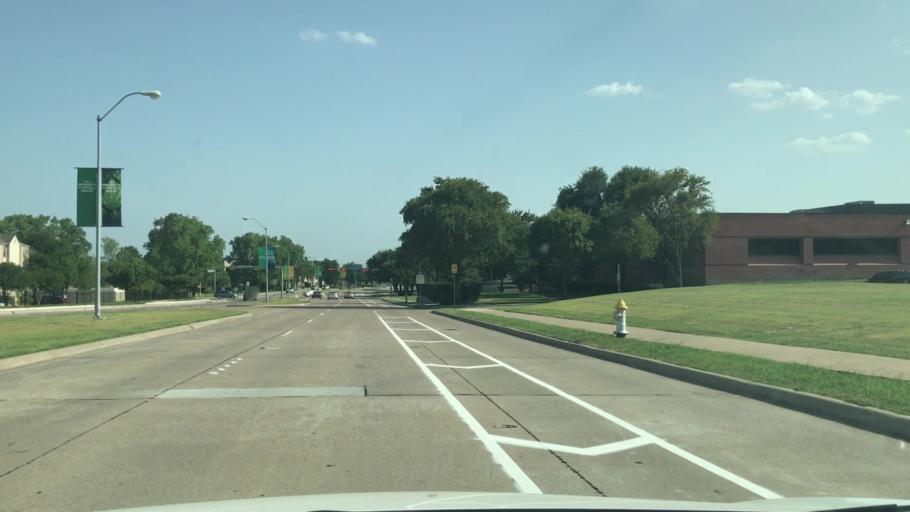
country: US
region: Texas
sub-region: Dallas County
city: Richardson
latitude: 32.9872
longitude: -96.7565
